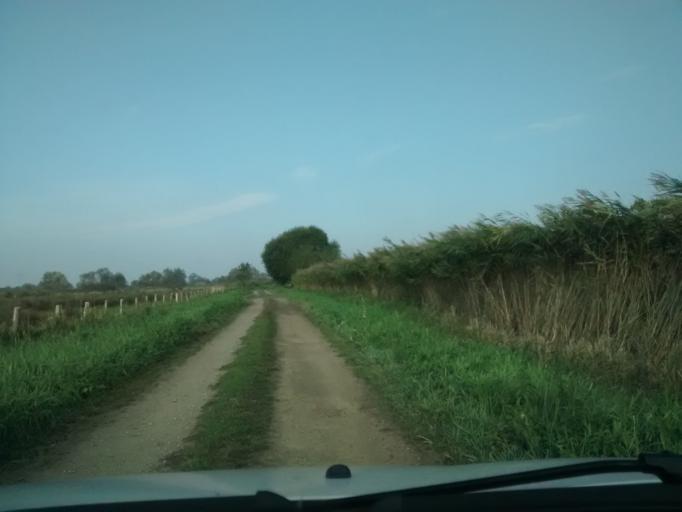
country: FR
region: Pays de la Loire
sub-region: Departement de la Loire-Atlantique
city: Cordemais
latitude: 47.2469
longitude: -1.8726
